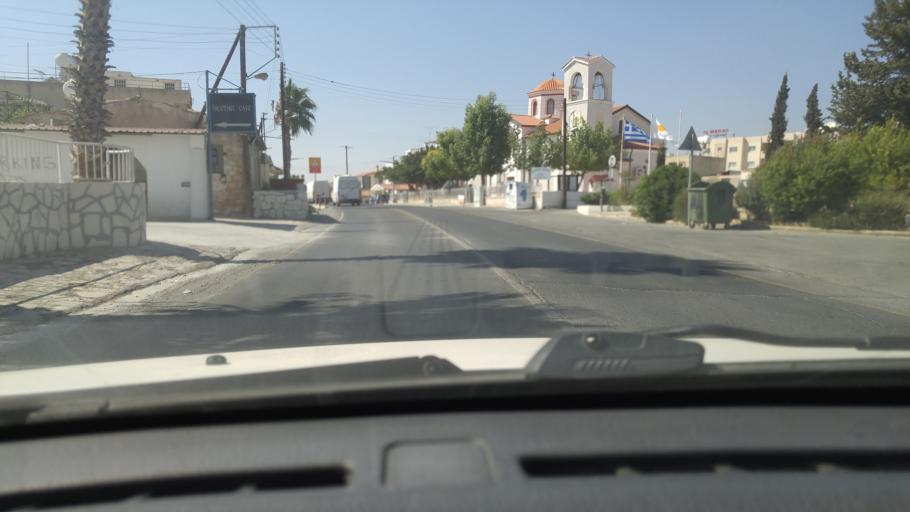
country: CY
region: Limassol
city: Ypsonas
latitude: 34.6842
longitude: 32.9647
